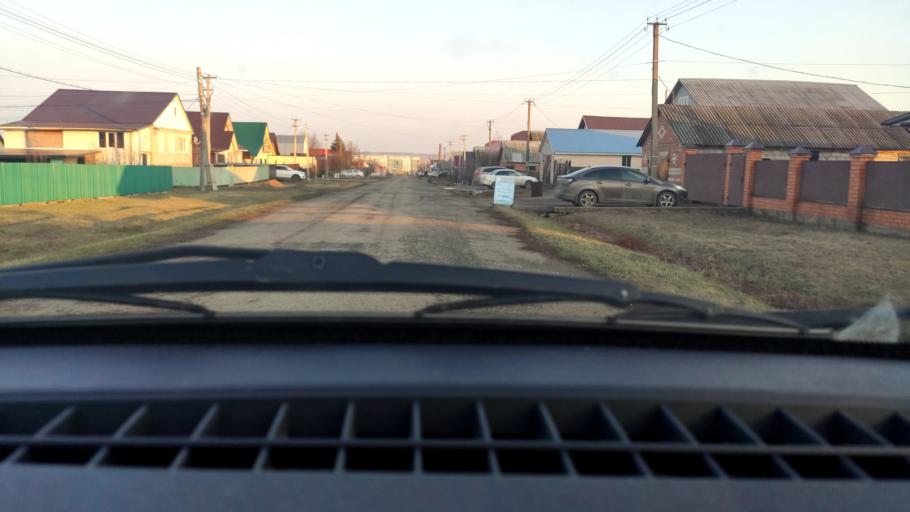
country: RU
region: Bashkortostan
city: Davlekanovo
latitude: 54.2336
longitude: 55.0274
